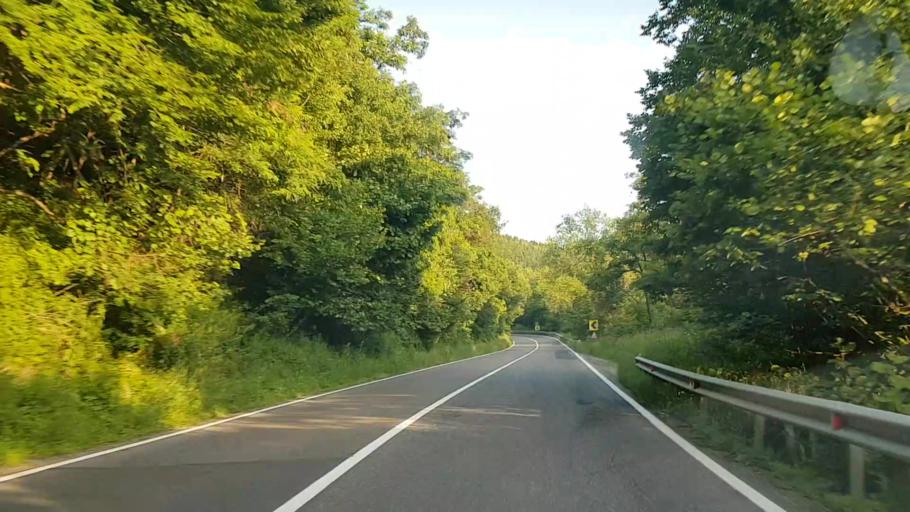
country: RO
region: Harghita
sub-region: Comuna Corund
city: Corund
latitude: 46.4528
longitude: 25.2126
